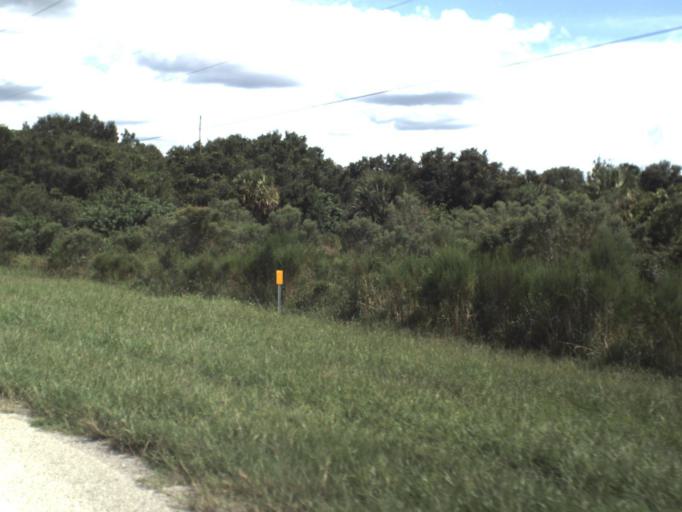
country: US
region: Florida
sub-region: Polk County
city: Bartow
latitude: 27.8981
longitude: -81.8863
